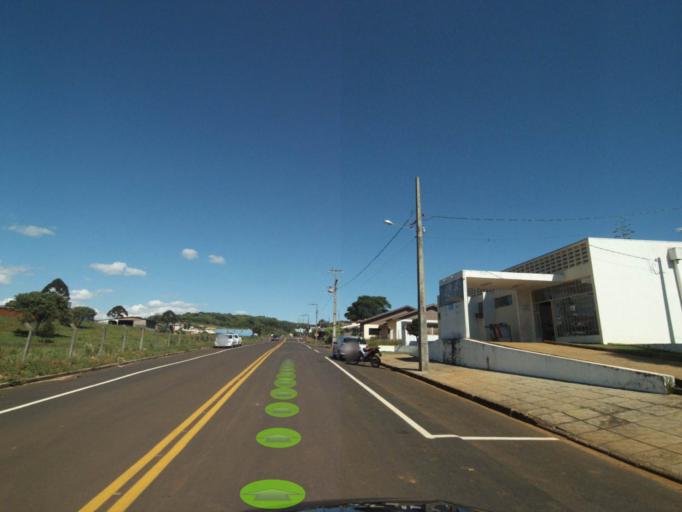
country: BR
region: Parana
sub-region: Coronel Vivida
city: Coronel Vivida
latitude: -26.1450
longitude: -52.3849
